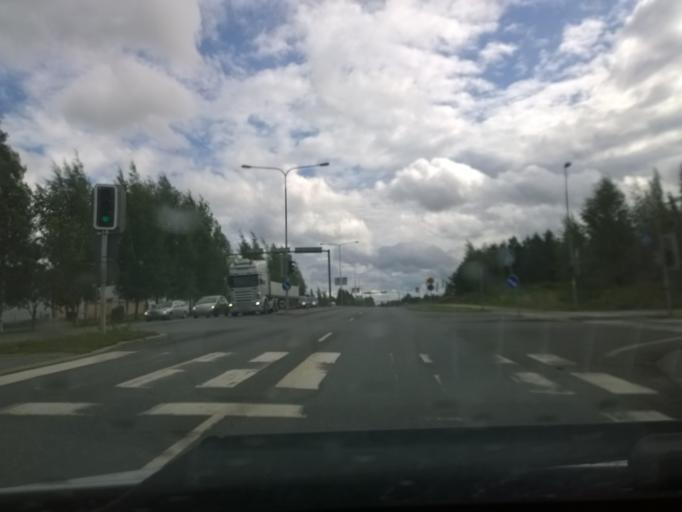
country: FI
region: Pirkanmaa
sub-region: Tampere
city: Tampere
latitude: 61.4783
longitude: 23.8670
